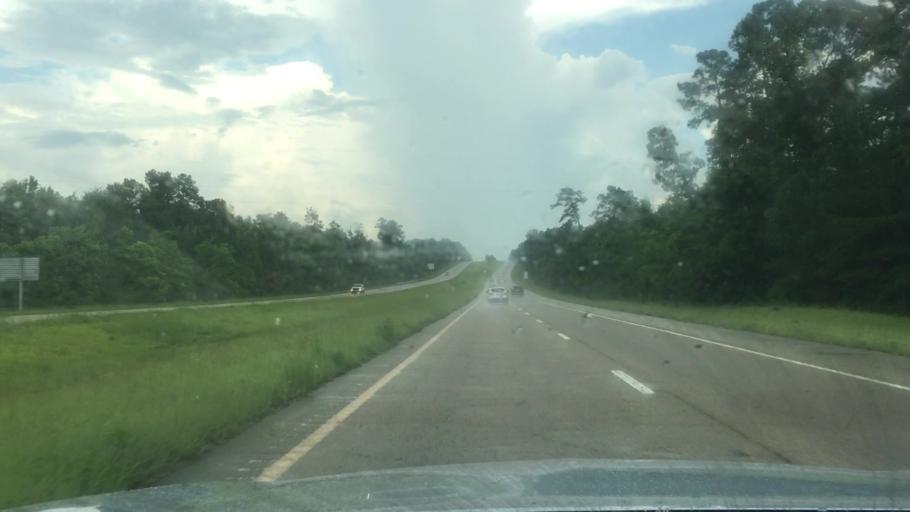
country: US
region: Mississippi
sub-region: Lamar County
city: Purvis
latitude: 31.1463
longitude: -89.3649
